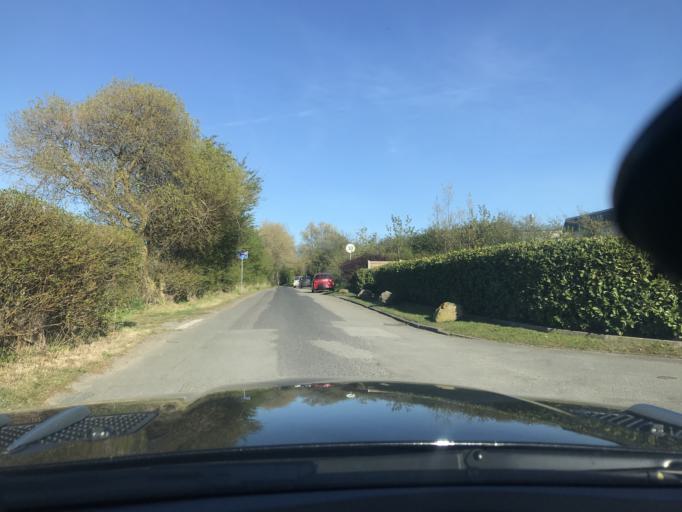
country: DE
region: Schleswig-Holstein
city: Grossenbrode
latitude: 54.3816
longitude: 11.0851
